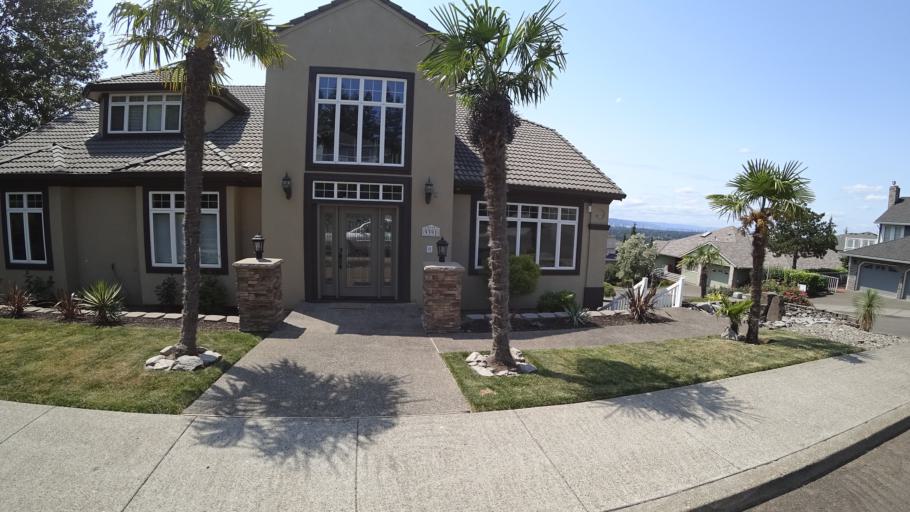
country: US
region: Oregon
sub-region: Multnomah County
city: Lents
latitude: 45.4535
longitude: -122.5640
